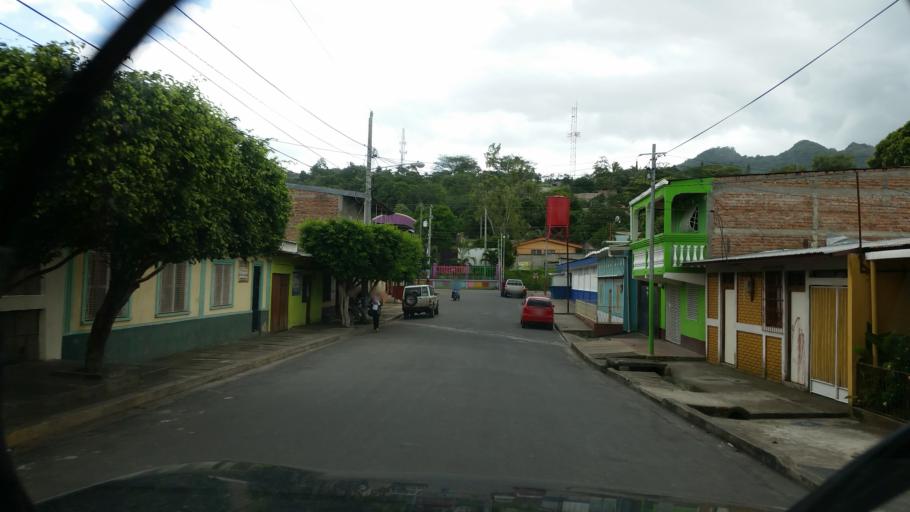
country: NI
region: Matagalpa
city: Matagalpa
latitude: 12.9308
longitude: -85.9131
